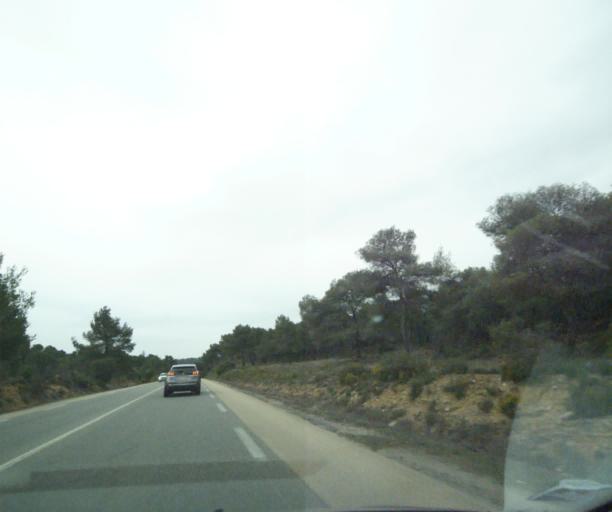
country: FR
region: Provence-Alpes-Cote d'Azur
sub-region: Departement des Bouches-du-Rhone
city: Venelles
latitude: 43.6157
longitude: 5.5039
